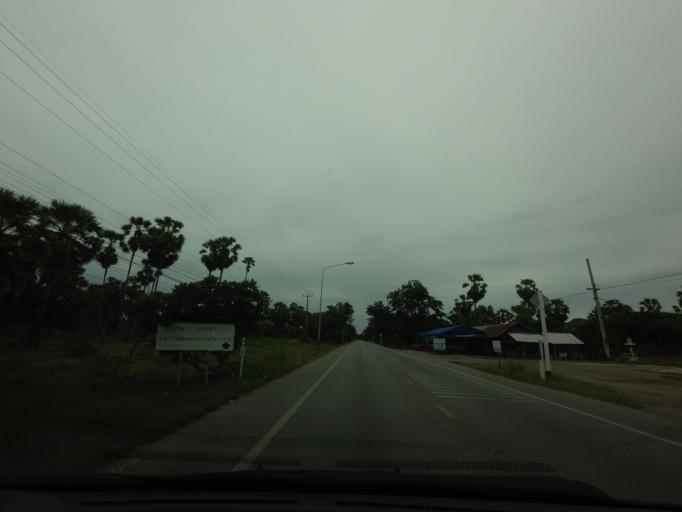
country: TH
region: Phetchaburi
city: Cha-am
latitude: 12.8409
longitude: 99.9957
